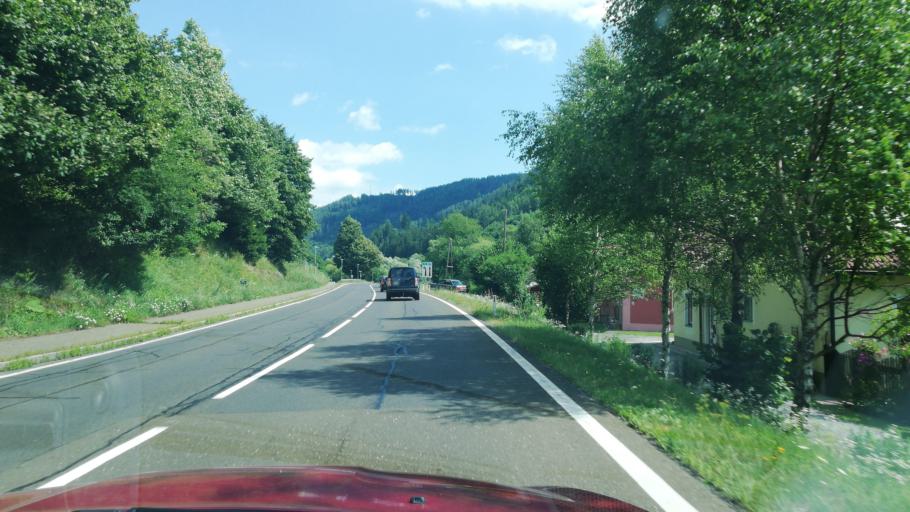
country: AT
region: Styria
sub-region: Politischer Bezirk Murau
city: Durnstein in der Steiermark
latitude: 47.0171
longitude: 14.4104
